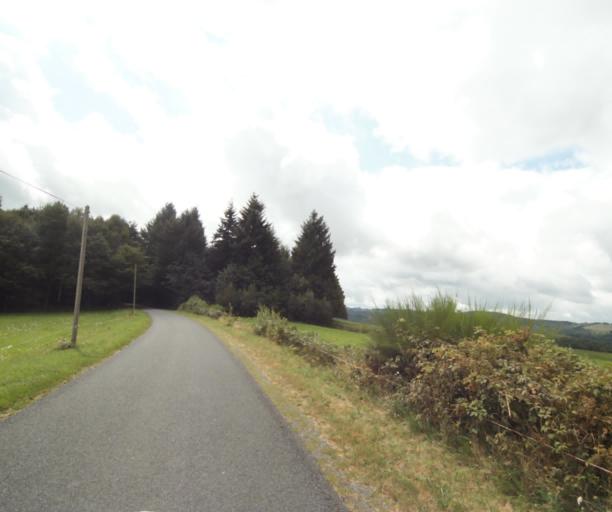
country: FR
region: Limousin
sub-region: Departement de la Correze
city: Sainte-Fortunade
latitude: 45.1681
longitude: 1.8030
